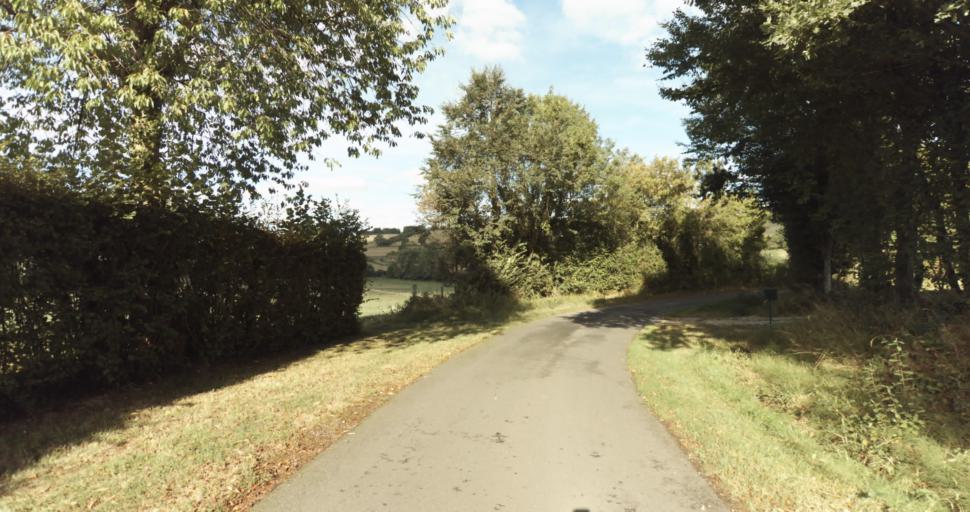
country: FR
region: Lower Normandy
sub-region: Departement de l'Orne
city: Vimoutiers
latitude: 48.9200
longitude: 0.1281
